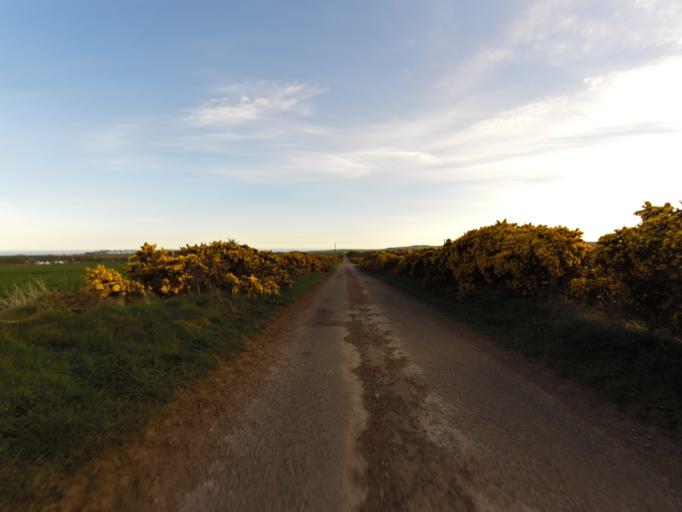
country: GB
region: Scotland
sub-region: Aberdeenshire
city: Stonehaven
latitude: 56.9178
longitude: -2.2273
